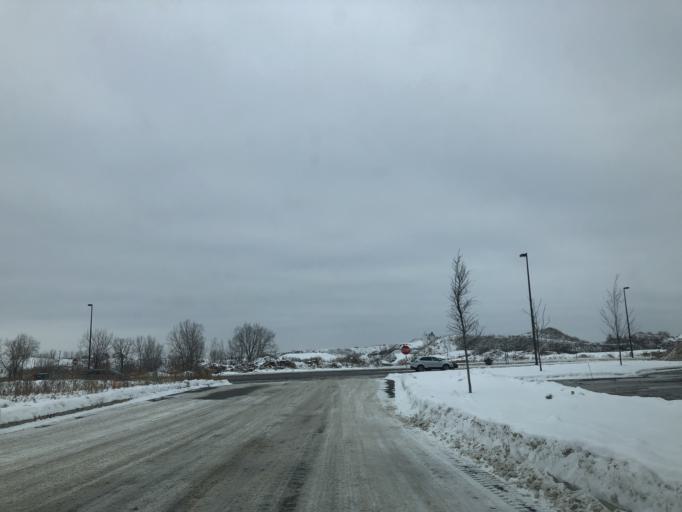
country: US
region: Minnesota
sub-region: Hennepin County
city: Osseo
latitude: 45.0941
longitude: -93.4169
